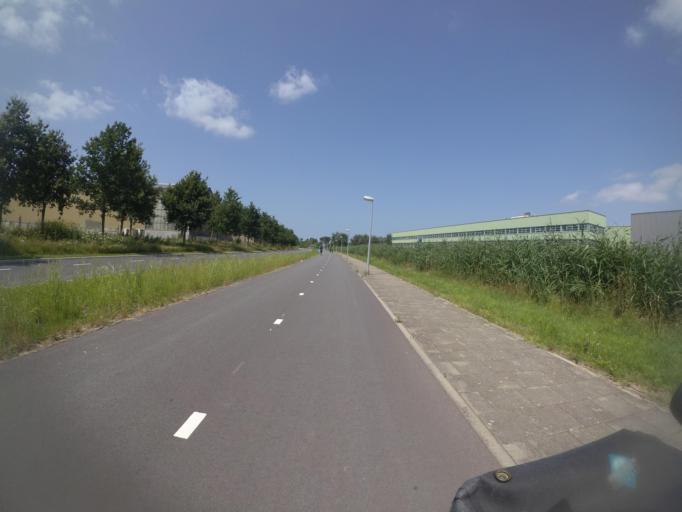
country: NL
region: Flevoland
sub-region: Gemeente Almere
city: Almere Stad
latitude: 52.3653
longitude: 5.2714
